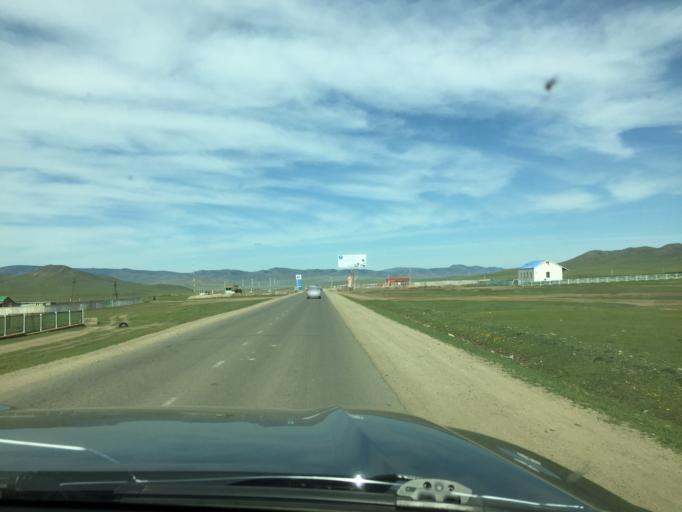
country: MN
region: Central Aimak
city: Ihsueuej
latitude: 48.2276
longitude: 106.2878
